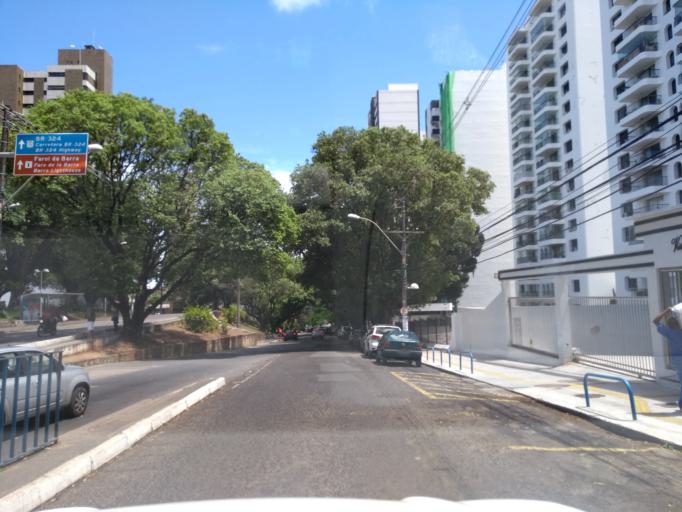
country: BR
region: Bahia
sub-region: Salvador
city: Salvador
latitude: -12.9995
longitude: -38.5241
